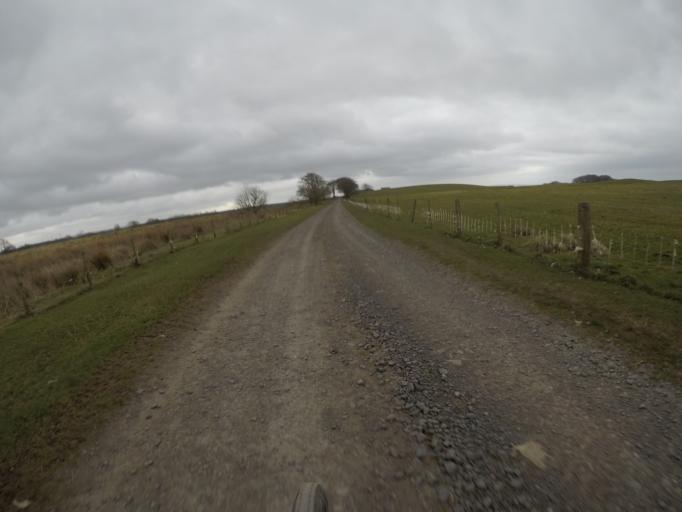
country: GB
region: Scotland
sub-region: East Ayrshire
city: Galston
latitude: 55.6699
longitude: -4.3731
